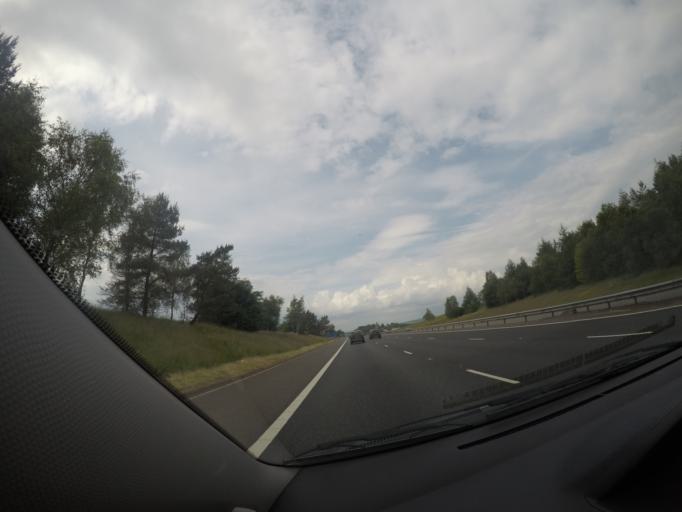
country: GB
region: Scotland
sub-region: Dumfries and Galloway
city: Lockerbie
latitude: 55.1242
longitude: -3.3647
